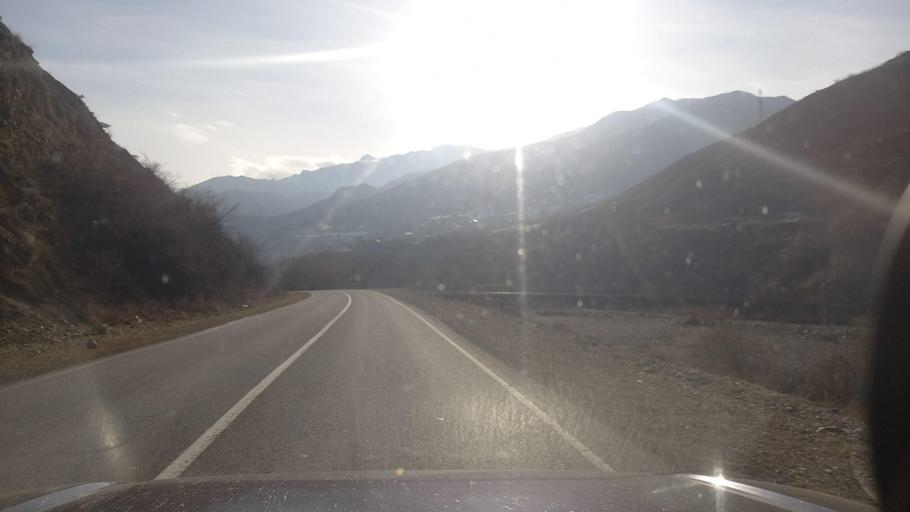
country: RU
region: Ingushetiya
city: Dzhayrakh
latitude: 42.8381
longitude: 44.6597
